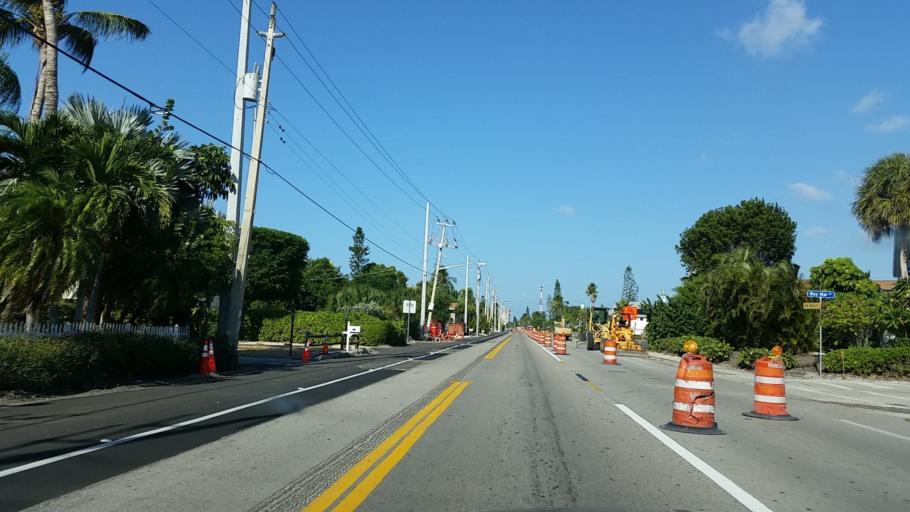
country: US
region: Florida
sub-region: Lee County
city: Fort Myers Beach
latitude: 26.4408
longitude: -81.9277
